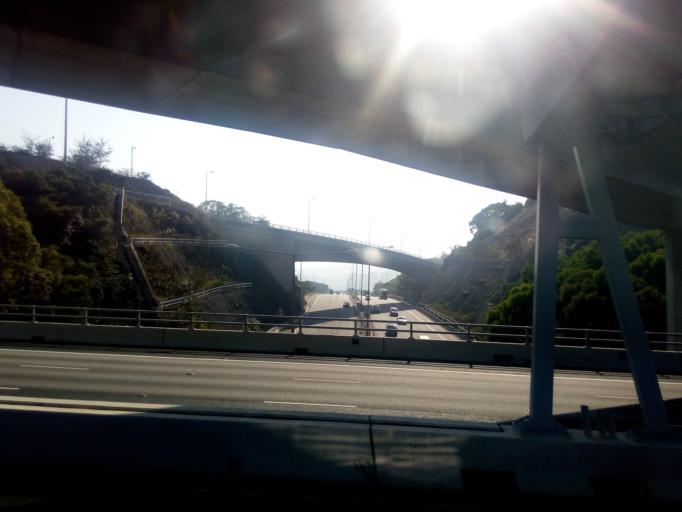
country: HK
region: Tsuen Wan
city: Tsuen Wan
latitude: 22.3713
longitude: 114.0740
